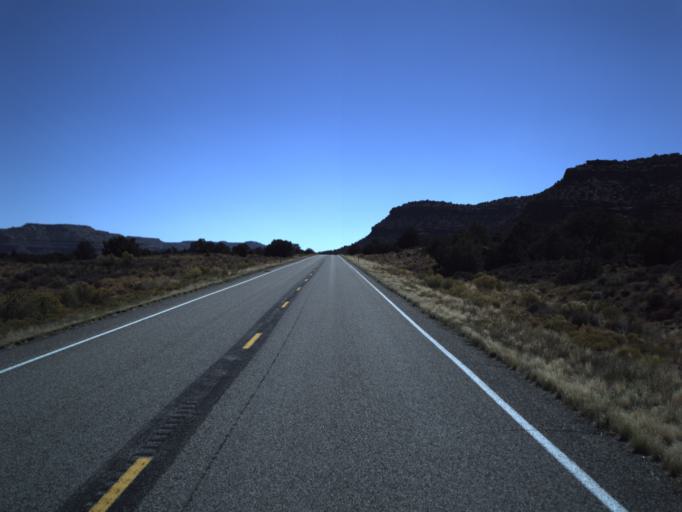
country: US
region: Utah
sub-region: San Juan County
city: Blanding
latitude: 37.6662
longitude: -110.1948
